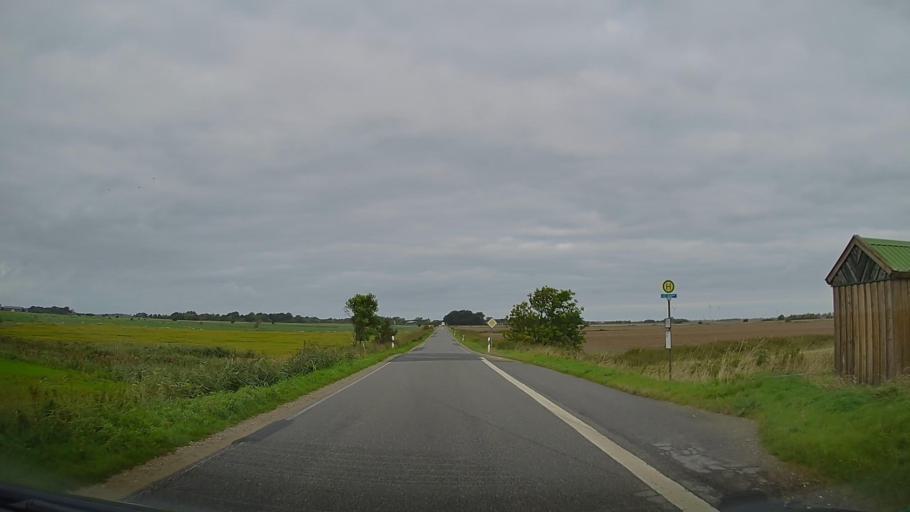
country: DE
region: Schleswig-Holstein
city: Emmelsbull-Horsbull
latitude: 54.8009
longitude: 8.7155
